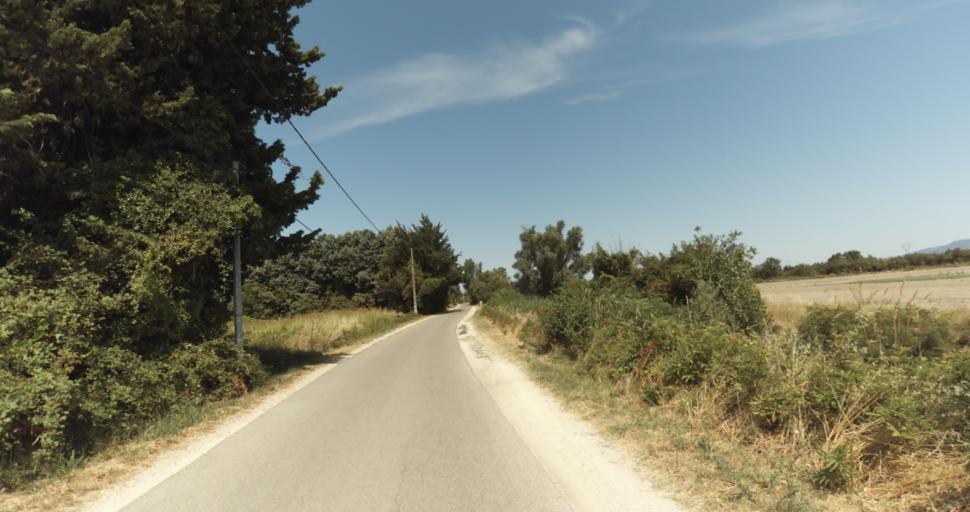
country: FR
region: Provence-Alpes-Cote d'Azur
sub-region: Departement du Vaucluse
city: Monteux
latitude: 44.0162
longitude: 4.9820
